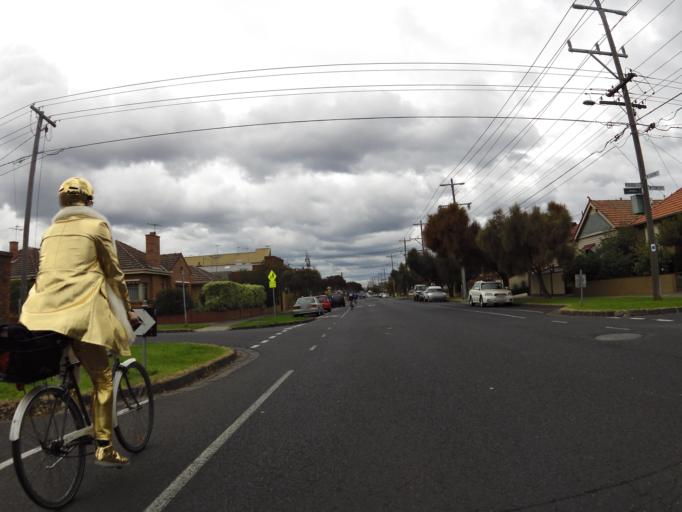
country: AU
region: Victoria
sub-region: Moreland
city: Coburg
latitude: -37.7454
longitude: 144.9699
